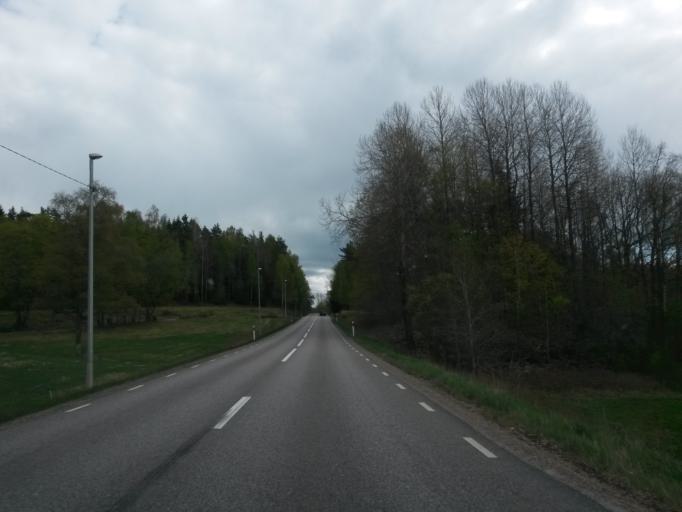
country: SE
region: Vaestra Goetaland
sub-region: Vargarda Kommun
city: Vargarda
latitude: 57.9010
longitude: 12.9128
